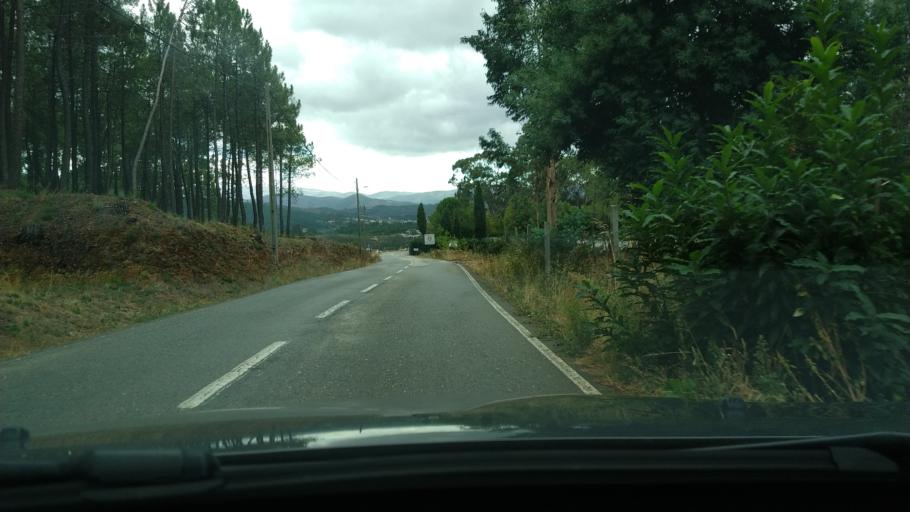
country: PT
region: Castelo Branco
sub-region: Covilha
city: Covilha
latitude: 40.2302
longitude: -7.6481
